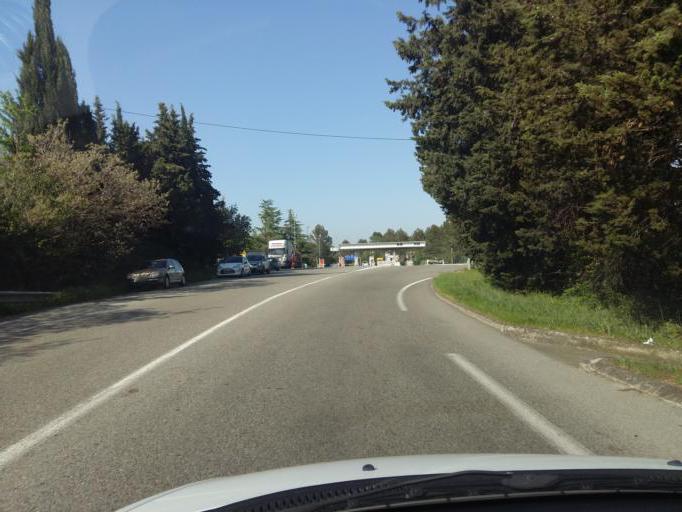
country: FR
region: Provence-Alpes-Cote d'Azur
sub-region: Departement du Var
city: Brignoles
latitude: 43.4181
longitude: 6.0636
